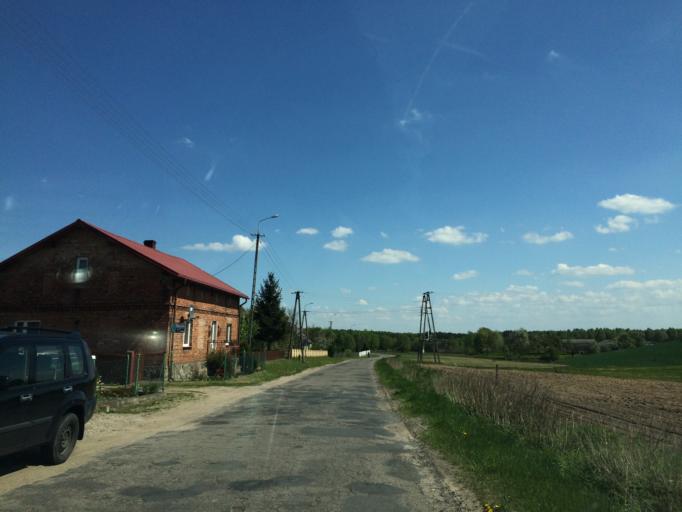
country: PL
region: Warmian-Masurian Voivodeship
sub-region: Powiat nowomiejski
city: Kurzetnik
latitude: 53.3850
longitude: 19.4711
